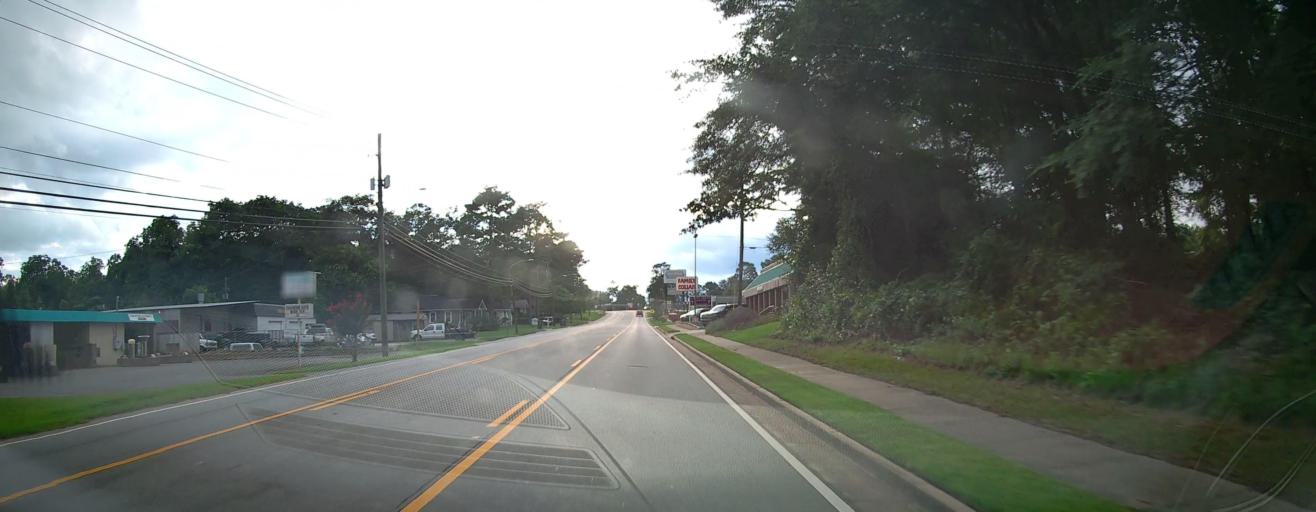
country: US
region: Georgia
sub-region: Houston County
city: Perry
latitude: 32.4591
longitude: -83.7228
